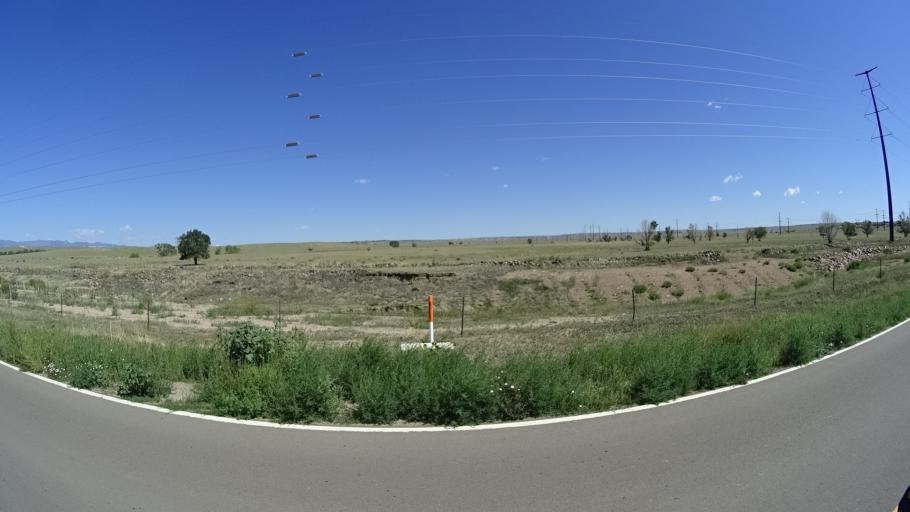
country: US
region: Colorado
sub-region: El Paso County
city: Security-Widefield
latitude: 38.7810
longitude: -104.6348
